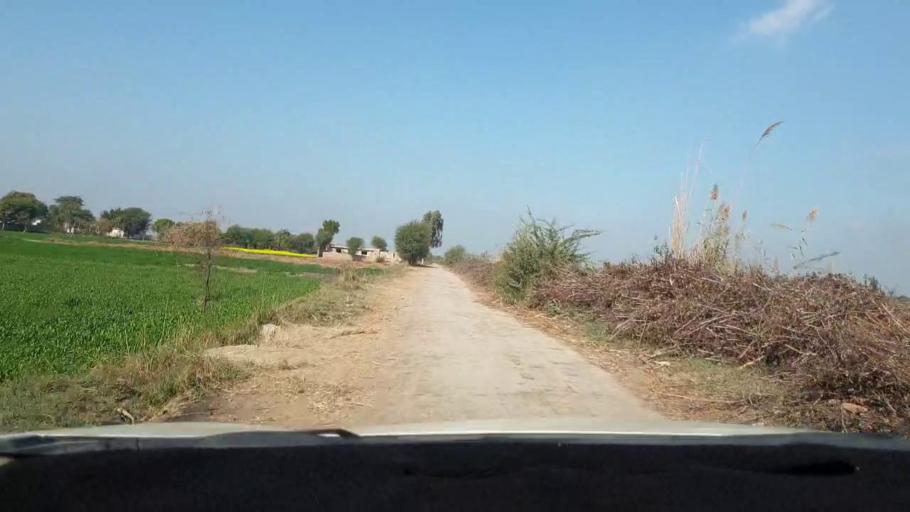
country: PK
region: Sindh
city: Berani
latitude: 25.8030
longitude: 68.8364
